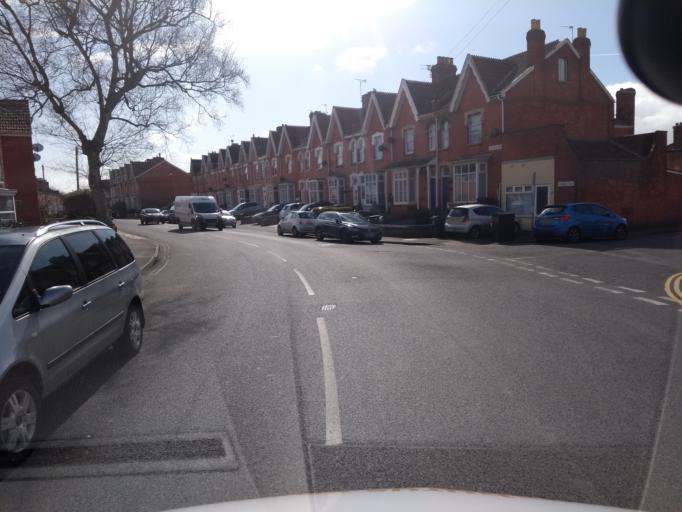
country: GB
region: England
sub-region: Somerset
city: Bridgwater
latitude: 51.1313
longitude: -3.0139
